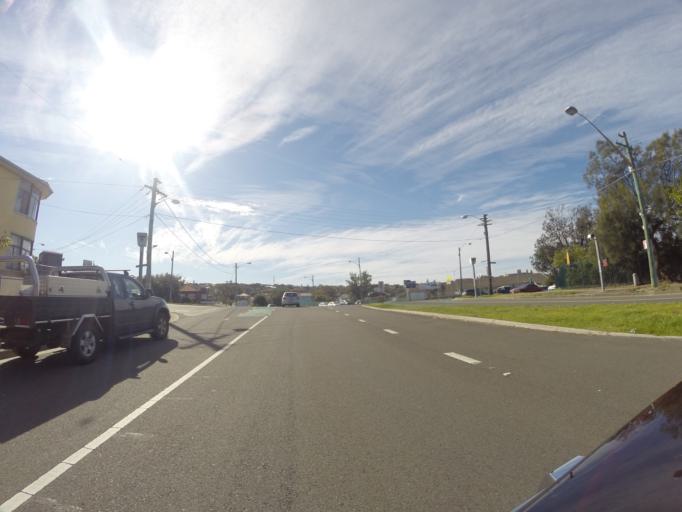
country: AU
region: New South Wales
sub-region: Randwick
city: Malabar
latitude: -33.9469
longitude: 151.2517
